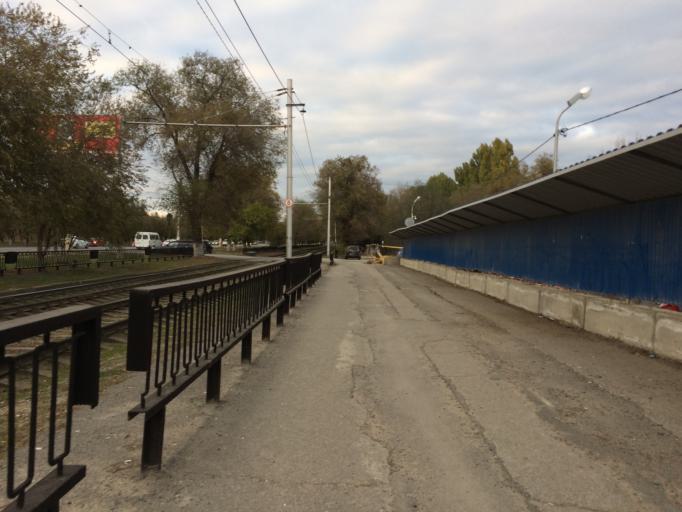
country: RU
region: Volgograd
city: Krasnoslobodsk
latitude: 48.7369
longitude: 44.5454
